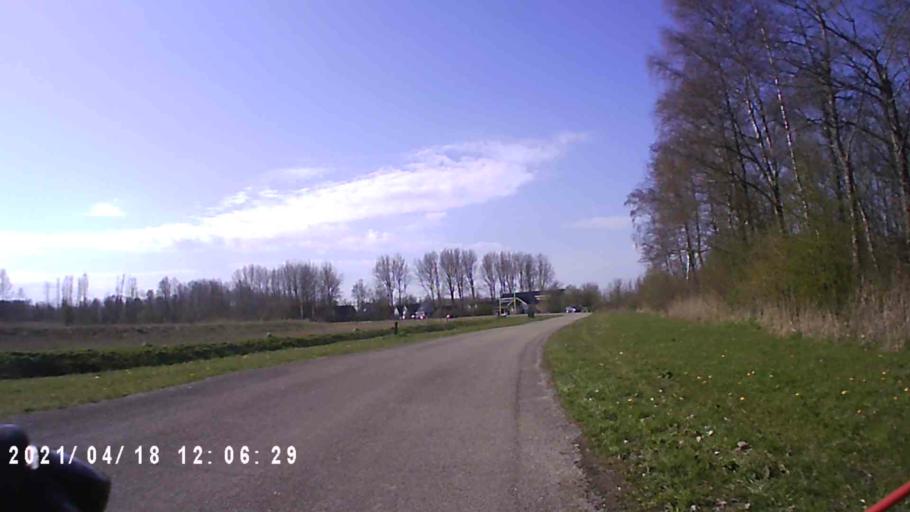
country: NL
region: Friesland
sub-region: Gemeente Kollumerland en Nieuwkruisland
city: Kollum
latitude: 53.3272
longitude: 6.1878
